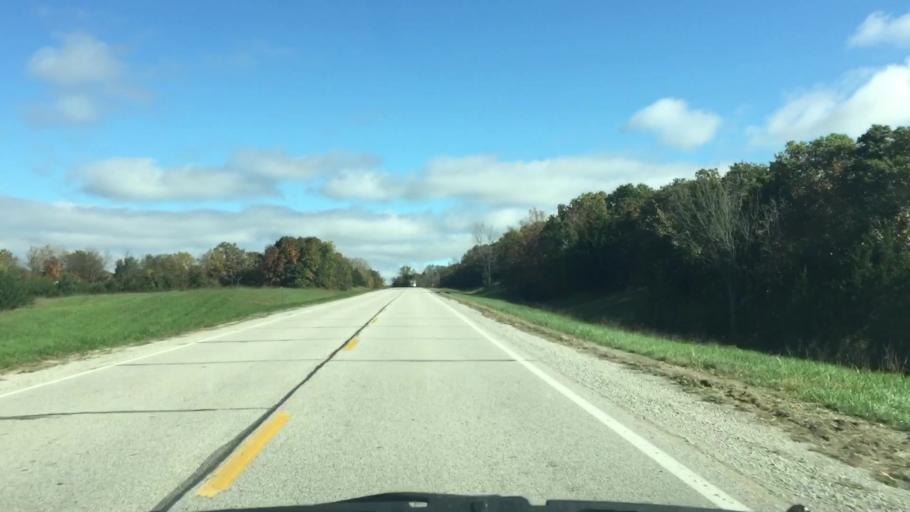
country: US
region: Iowa
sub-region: Decatur County
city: Leon
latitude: 40.6837
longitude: -93.7794
